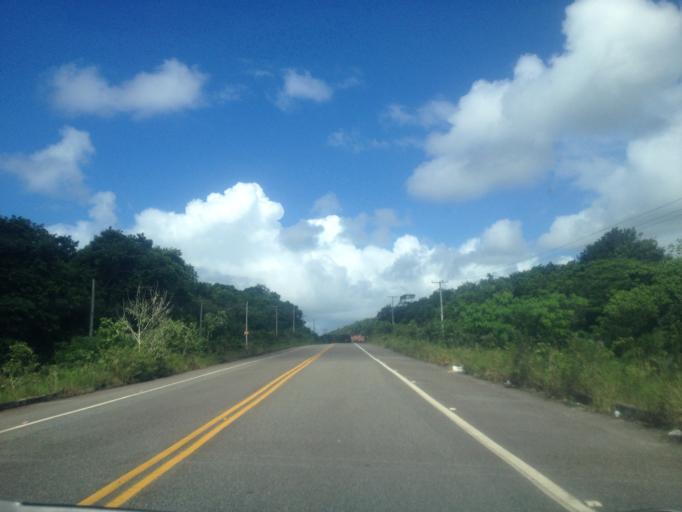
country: BR
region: Sergipe
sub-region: Indiaroba
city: Indiaroba
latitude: -11.4810
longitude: -37.4862
